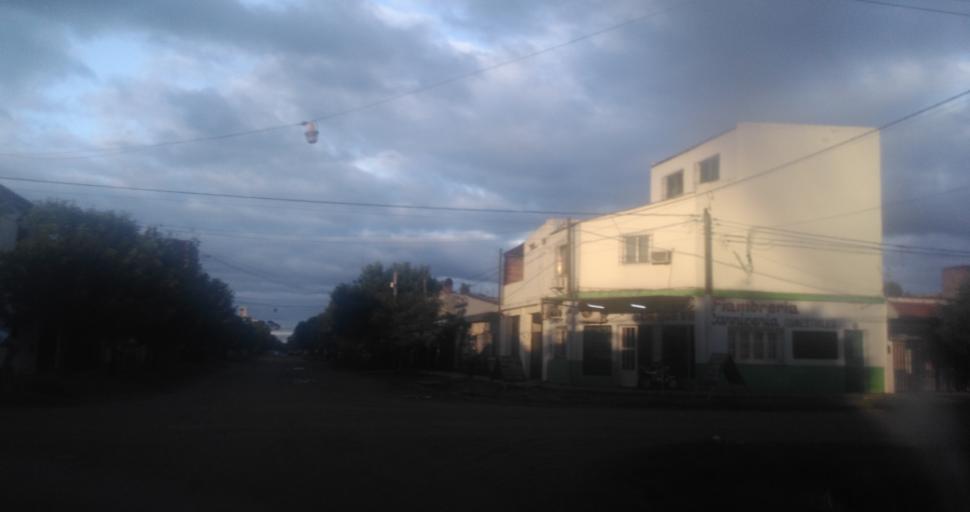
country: AR
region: Chaco
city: Resistencia
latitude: -27.4674
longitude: -58.9720
